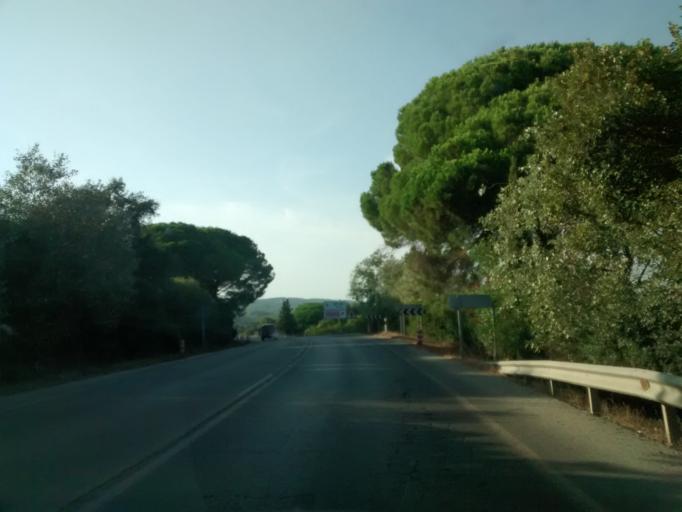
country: ES
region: Andalusia
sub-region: Provincia de Cadiz
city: Barbate de Franco
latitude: 36.2136
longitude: -5.9405
